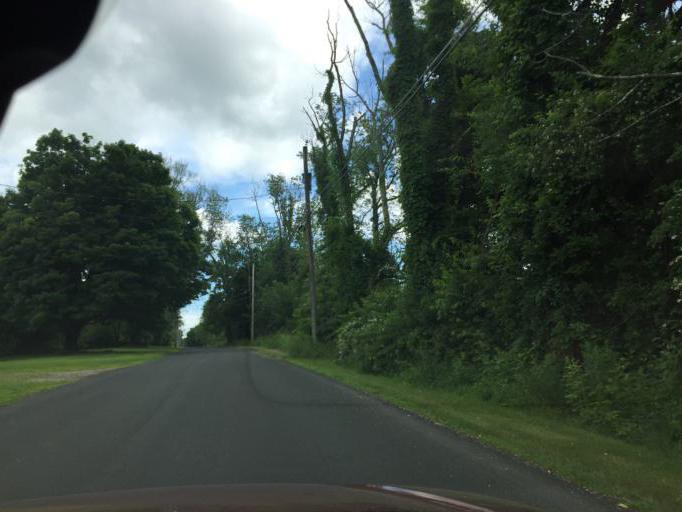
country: US
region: Connecticut
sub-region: Litchfield County
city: Litchfield
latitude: 41.7730
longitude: -73.2557
